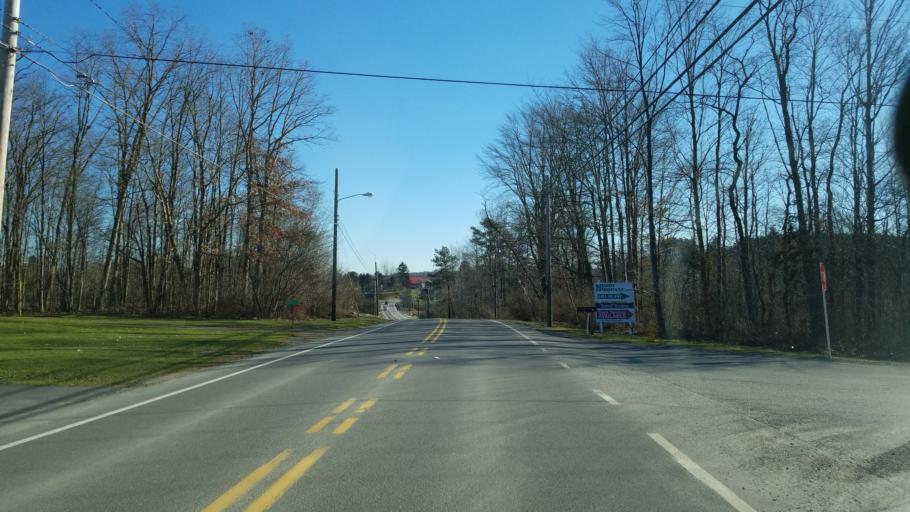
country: US
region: Pennsylvania
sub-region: Jefferson County
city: Falls Creek
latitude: 41.1488
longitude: -78.8112
